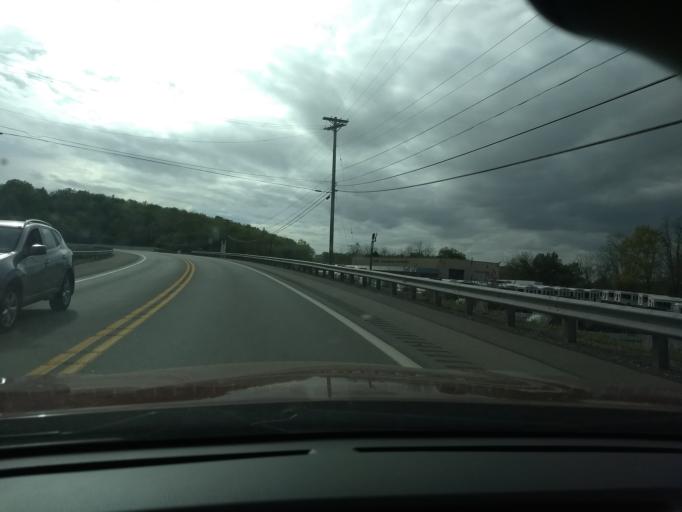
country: US
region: Pennsylvania
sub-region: Allegheny County
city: Russellton
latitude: 40.5829
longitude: -79.8709
